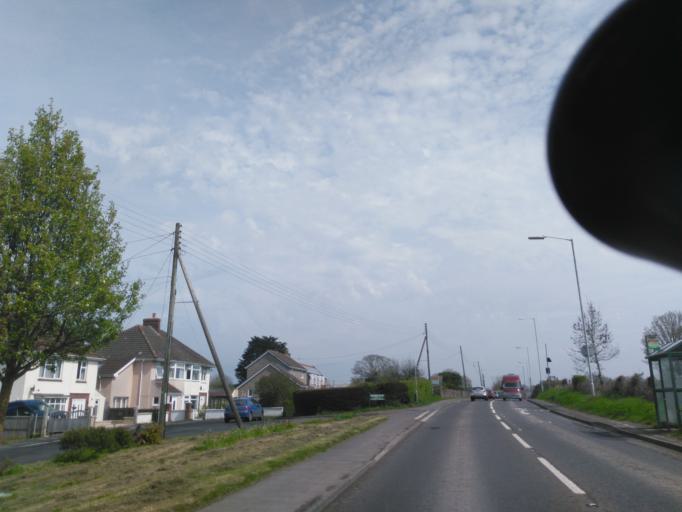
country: GB
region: England
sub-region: Somerset
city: Street
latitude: 51.1234
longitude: -2.7592
